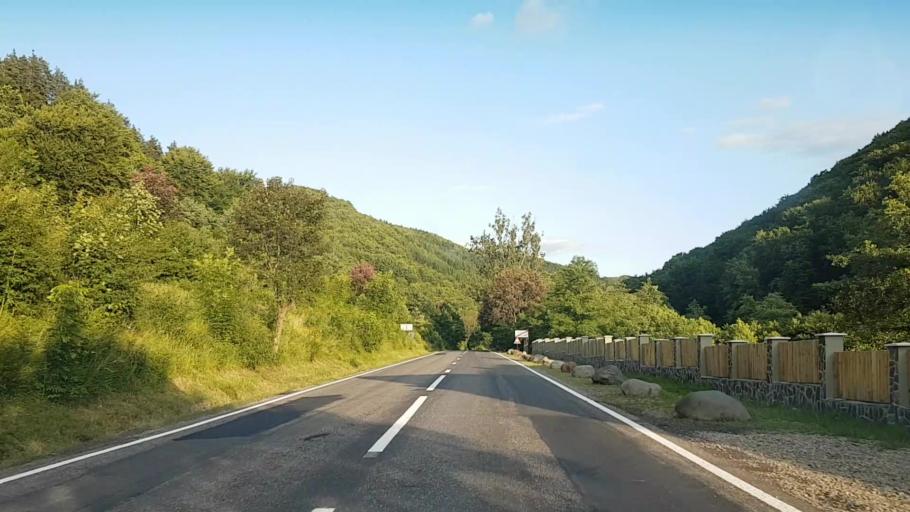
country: RO
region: Harghita
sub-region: Comuna Corund
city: Corund
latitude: 46.4655
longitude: 25.2051
